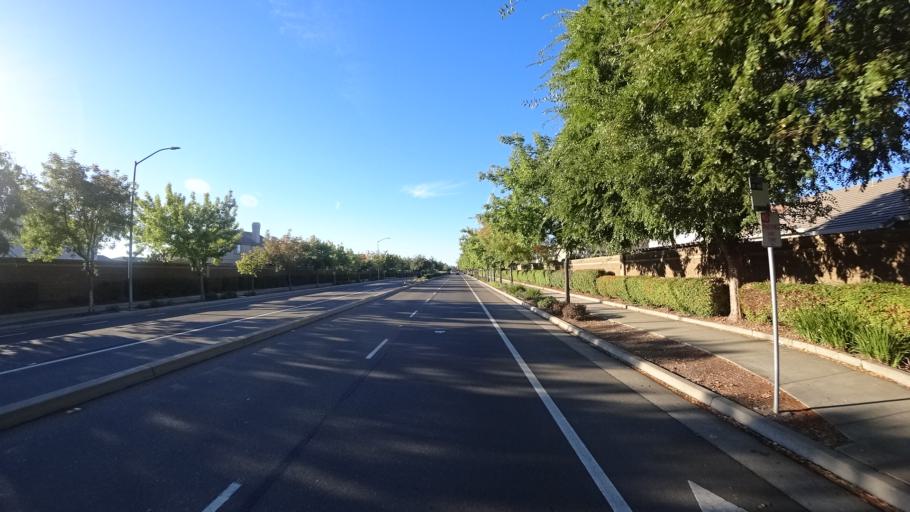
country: US
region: California
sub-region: Sacramento County
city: Laguna
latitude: 38.4441
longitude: -121.3921
